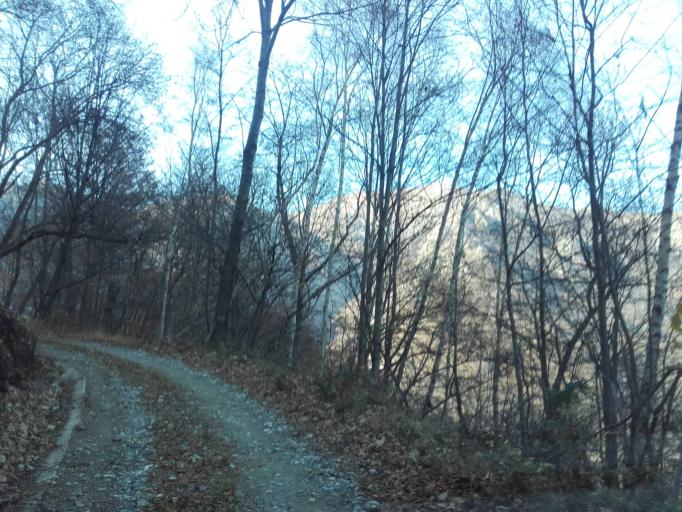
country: IT
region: Piedmont
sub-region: Provincia di Torino
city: Sparone
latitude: 45.4266
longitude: 7.5321
